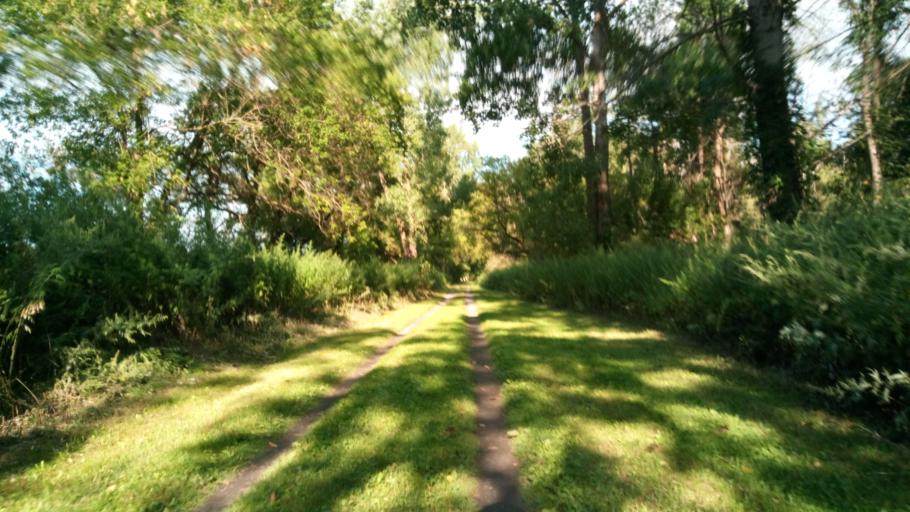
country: US
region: New York
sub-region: Monroe County
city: Honeoye Falls
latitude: 42.9912
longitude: -77.5326
